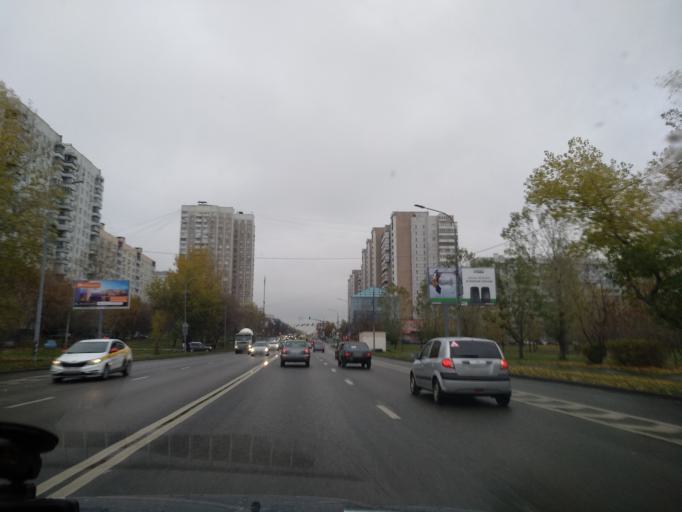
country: RU
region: Moscow
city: Kozeyevo
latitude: 55.8697
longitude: 37.6263
